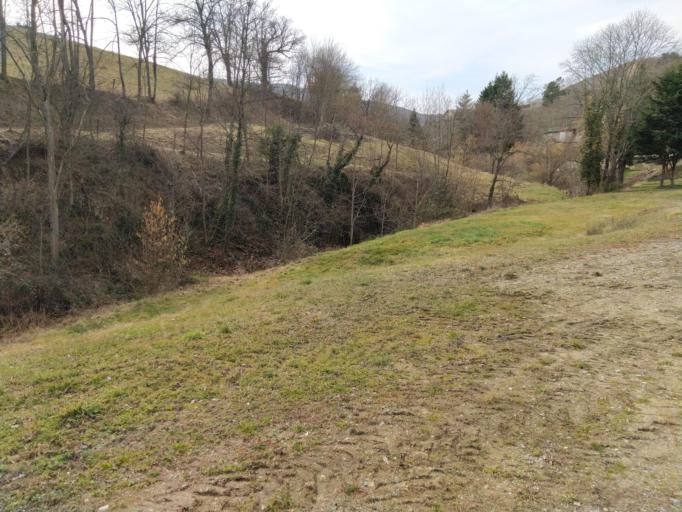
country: FR
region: Rhone-Alpes
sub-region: Departement de l'Ardeche
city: Saint-Marcel-les-Annonay
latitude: 45.2849
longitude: 4.6267
